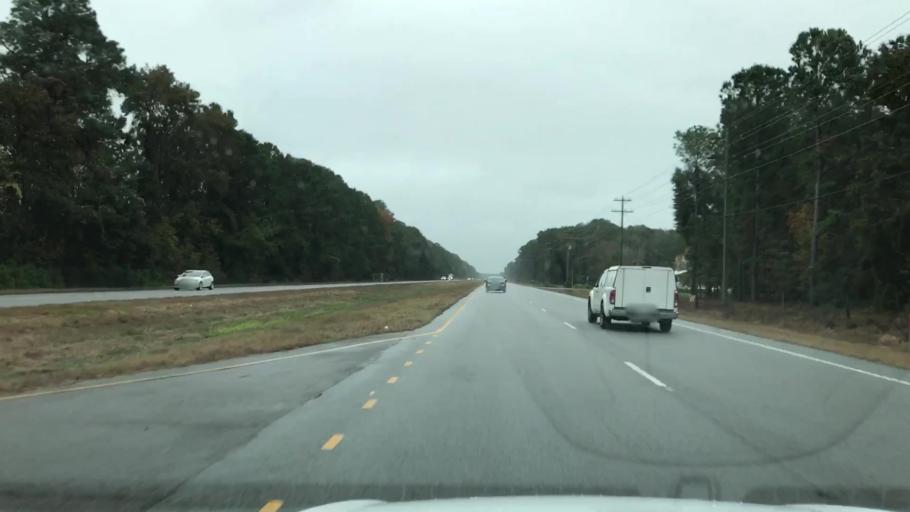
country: US
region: South Carolina
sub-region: Charleston County
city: Isle of Palms
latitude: 32.9003
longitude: -79.7311
